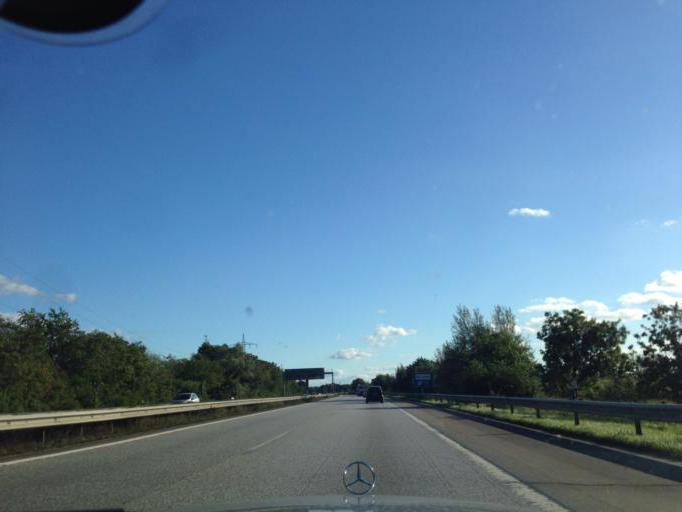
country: DE
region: Schleswig-Holstein
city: Padenstedt
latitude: 54.0629
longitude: 9.9225
